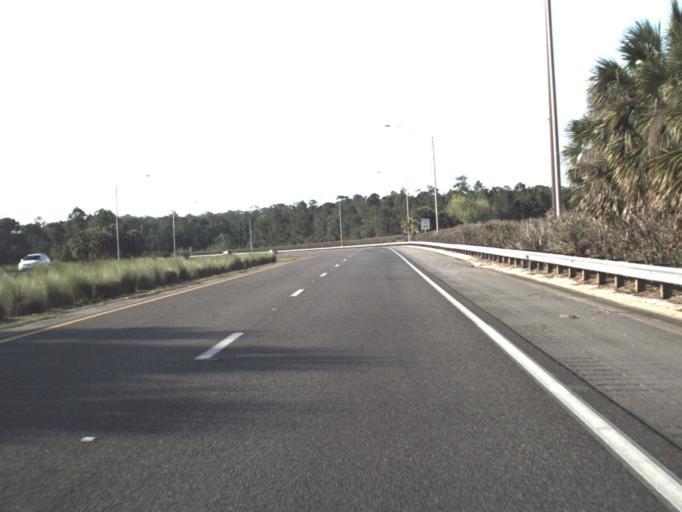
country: US
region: Florida
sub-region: Orange County
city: Alafaya
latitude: 28.5658
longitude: -81.1910
